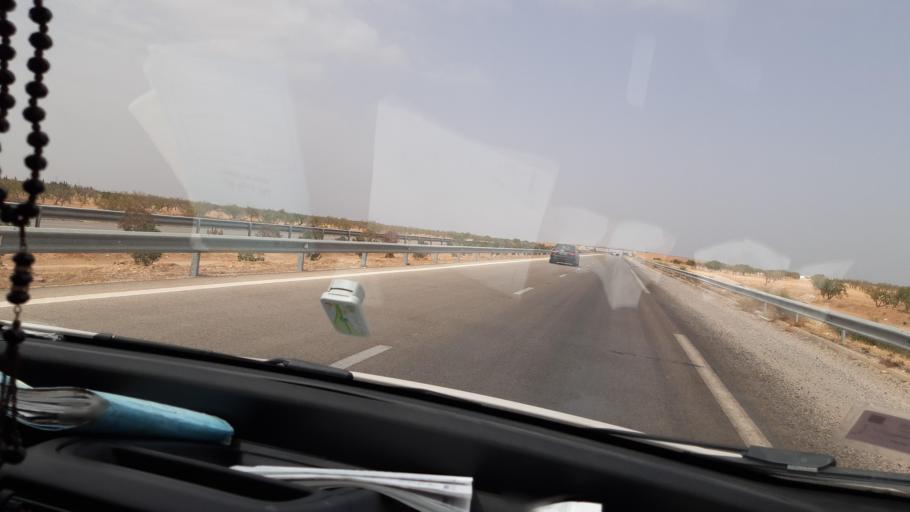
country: TN
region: Safaqis
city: Sfax
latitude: 34.8510
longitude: 10.6791
